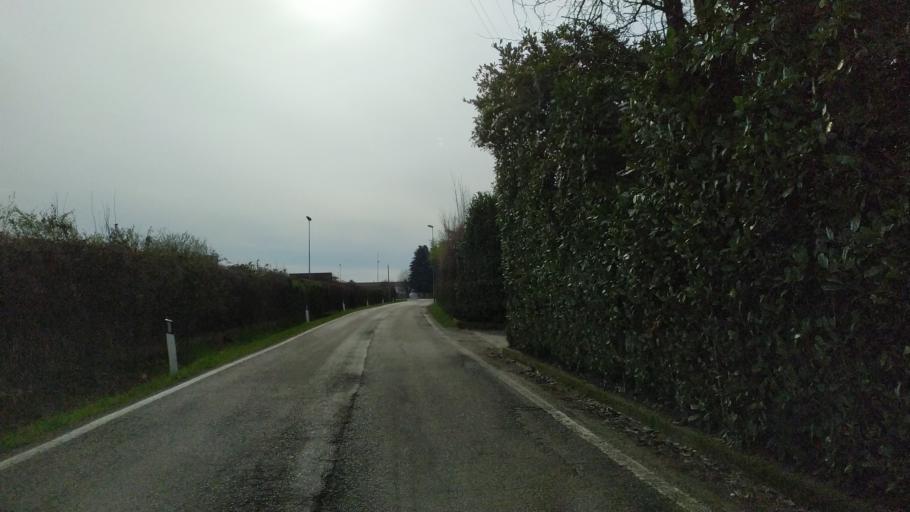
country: IT
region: Veneto
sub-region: Provincia di Vicenza
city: Villaverla
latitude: 45.6518
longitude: 11.4795
